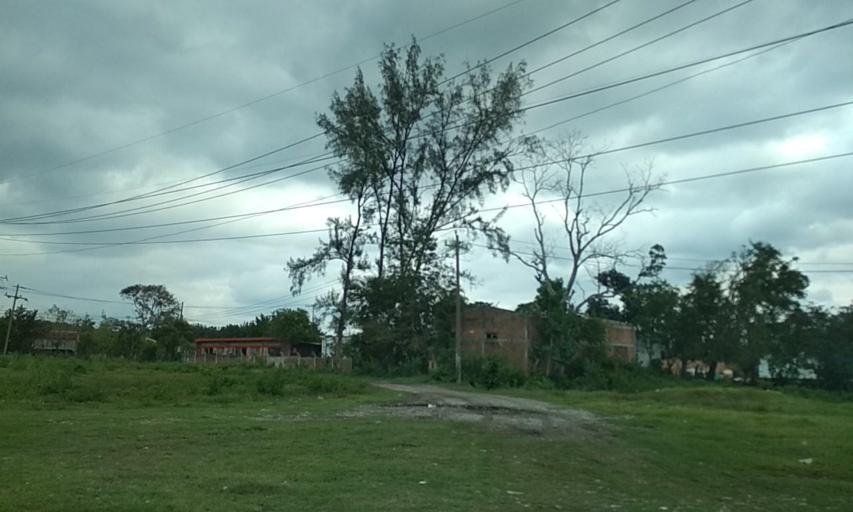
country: MX
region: Veracruz
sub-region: Papantla
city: El Chote
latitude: 20.3949
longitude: -97.3373
